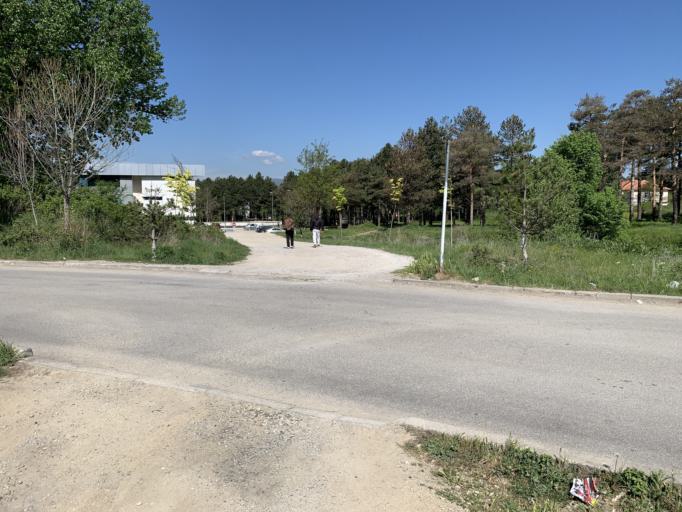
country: AL
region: Korce
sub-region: Rrethi i Korces
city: Korce
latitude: 40.6123
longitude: 20.7895
